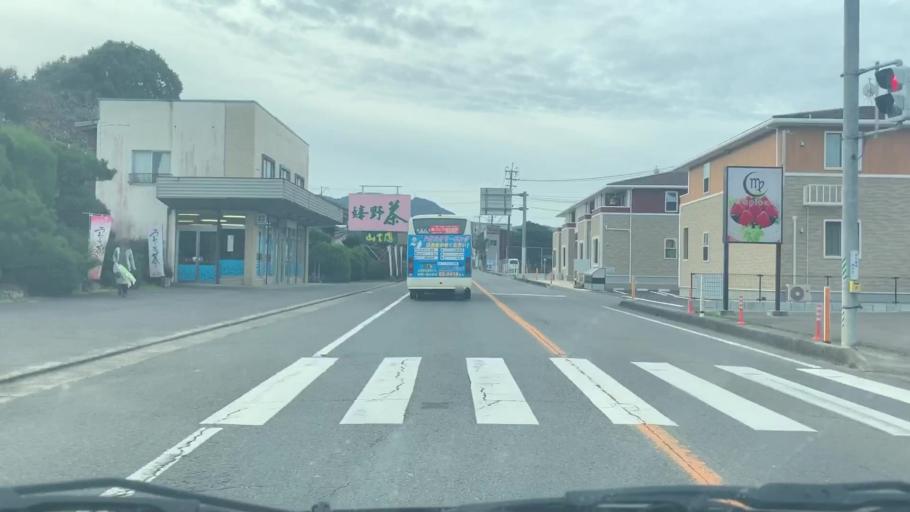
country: JP
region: Saga Prefecture
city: Ureshinomachi-shimojuku
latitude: 33.1146
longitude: 130.0014
